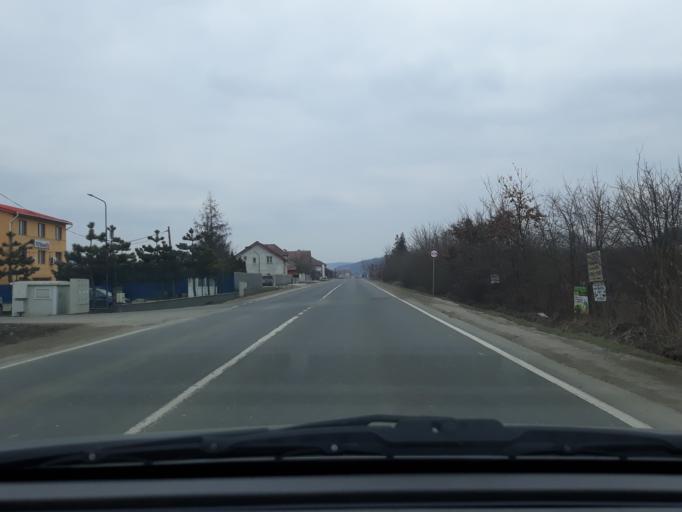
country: RO
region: Salaj
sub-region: Comuna Hereclean
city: Hereclean
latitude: 47.2253
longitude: 23.0113
